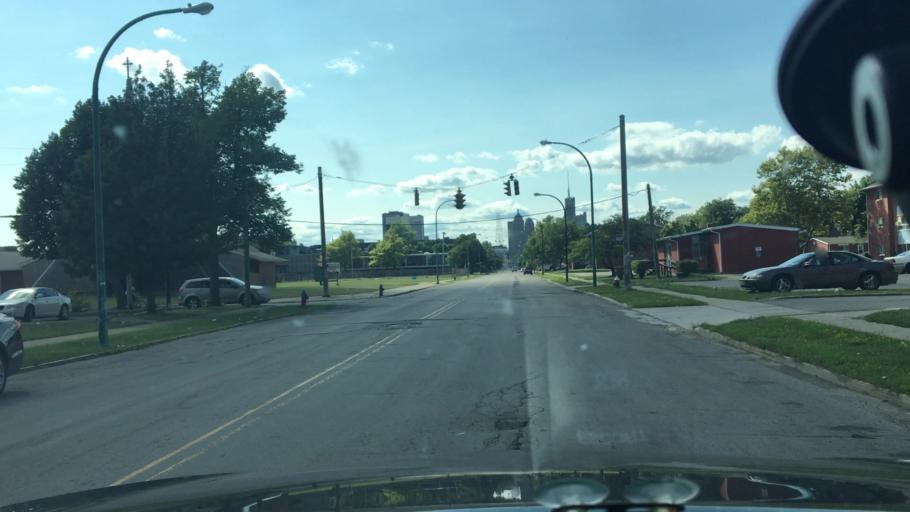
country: US
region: New York
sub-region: Erie County
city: Buffalo
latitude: 42.8823
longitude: -78.8560
